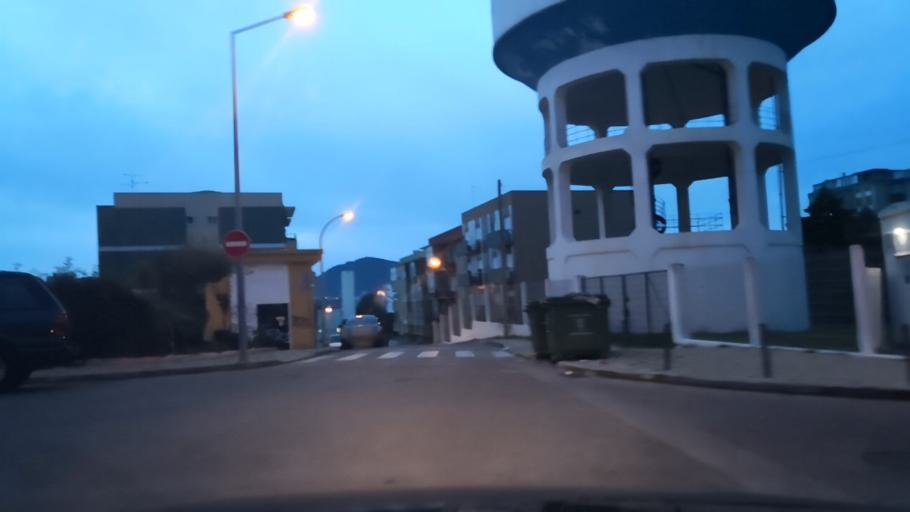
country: PT
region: Setubal
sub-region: Setubal
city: Setubal
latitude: 38.5291
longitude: -8.8778
